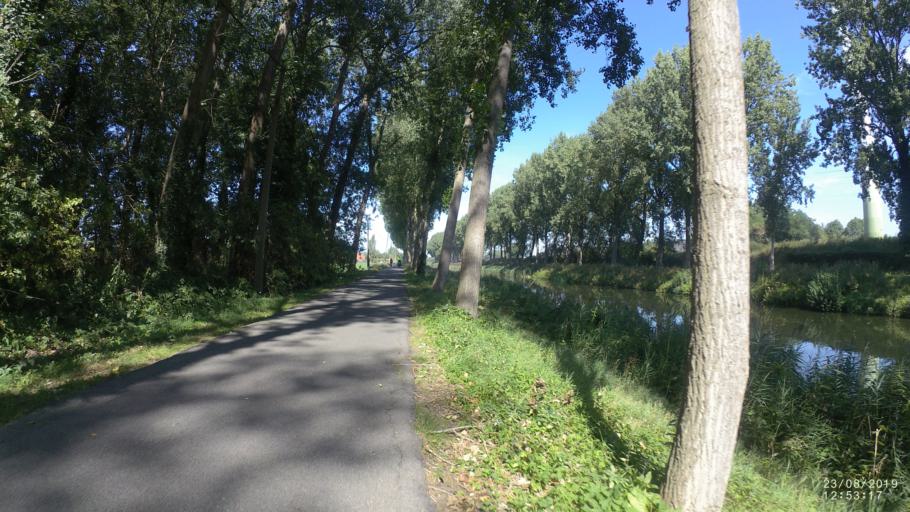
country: BE
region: Flanders
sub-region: Provincie Oost-Vlaanderen
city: Eeklo
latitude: 51.1807
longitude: 3.5312
